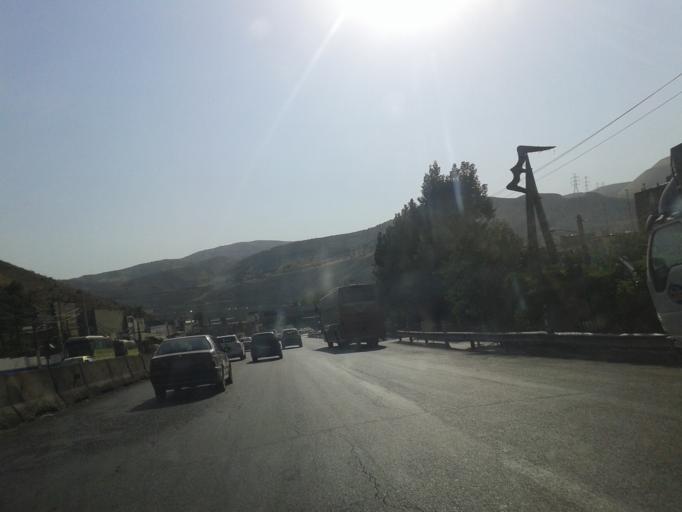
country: IR
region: Tehran
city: Pakdasht
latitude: 35.7428
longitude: 51.7002
